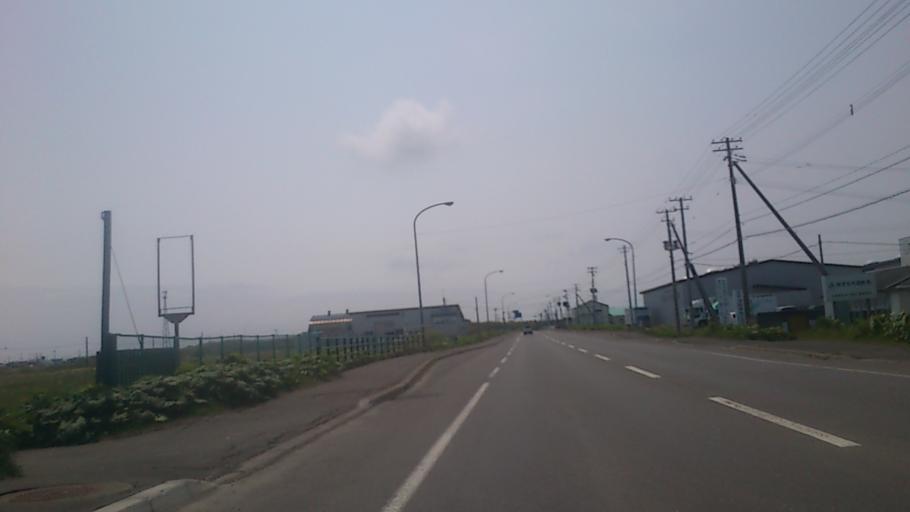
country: JP
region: Hokkaido
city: Nemuro
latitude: 43.3011
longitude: 145.5882
